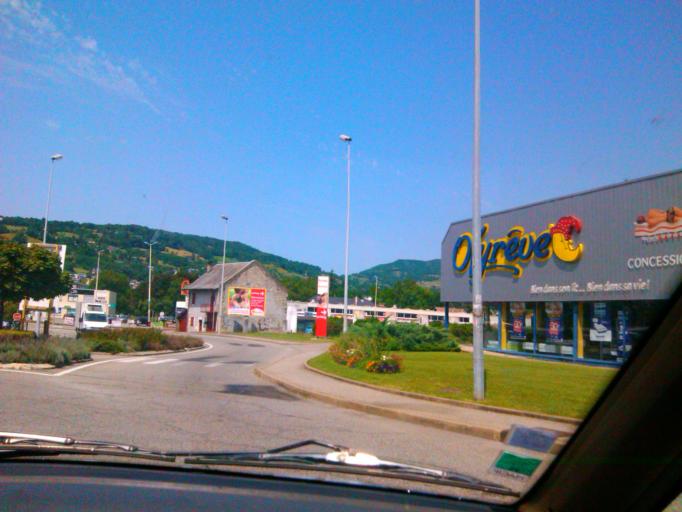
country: FR
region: Rhone-Alpes
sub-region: Departement de la Savoie
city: Saint-Alban-Leysse
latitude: 45.5735
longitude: 5.9470
